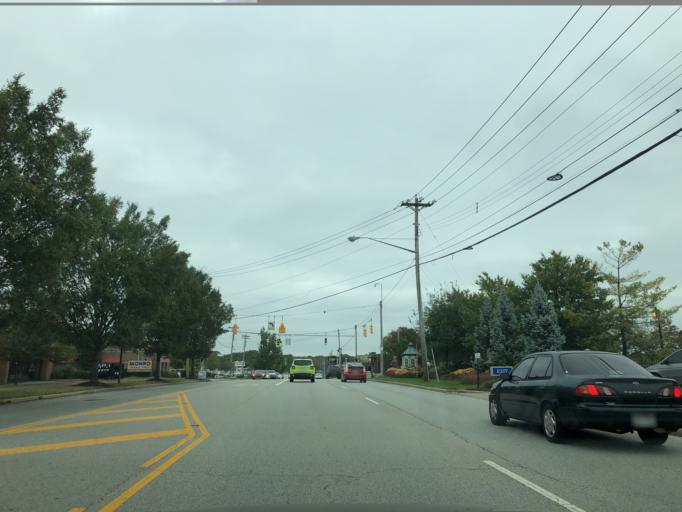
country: US
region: Ohio
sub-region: Hamilton County
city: Montgomery
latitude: 39.2344
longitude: -84.3511
